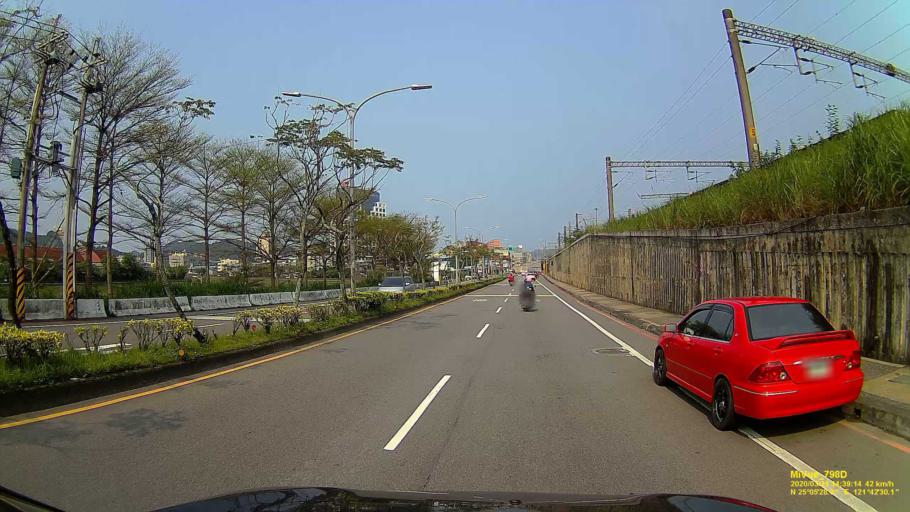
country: TW
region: Taiwan
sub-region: Keelung
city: Keelung
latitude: 25.0912
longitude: 121.7085
